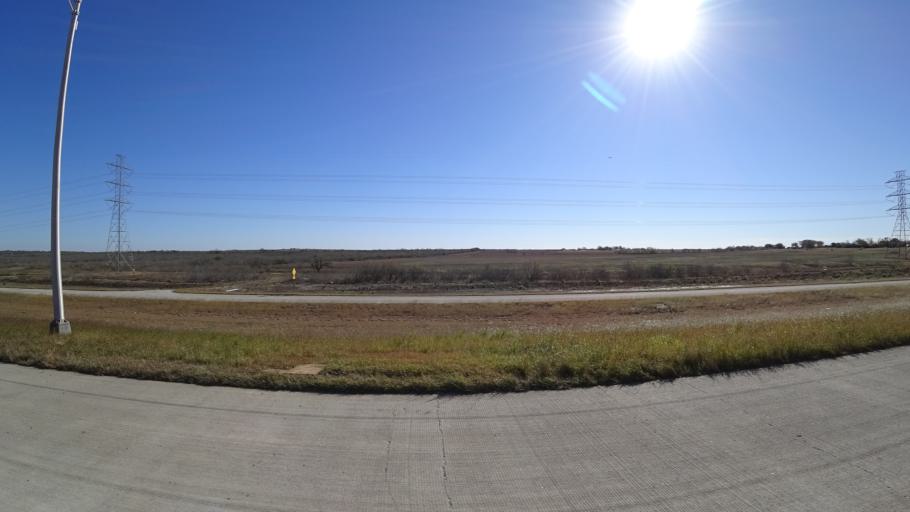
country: US
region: Texas
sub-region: Travis County
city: Onion Creek
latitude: 30.1059
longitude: -97.6666
